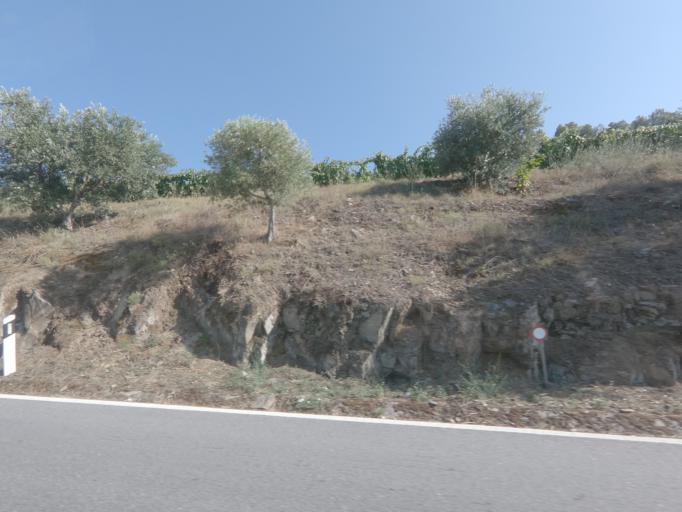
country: PT
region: Viseu
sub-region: Tabuaco
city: Tabuaco
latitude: 41.1403
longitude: -7.5663
